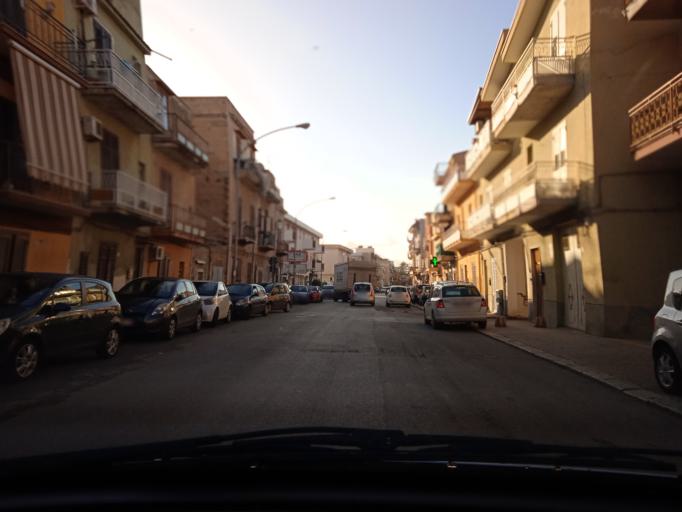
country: IT
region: Sicily
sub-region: Palermo
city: Ciaculli
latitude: 38.0902
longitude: 13.4171
